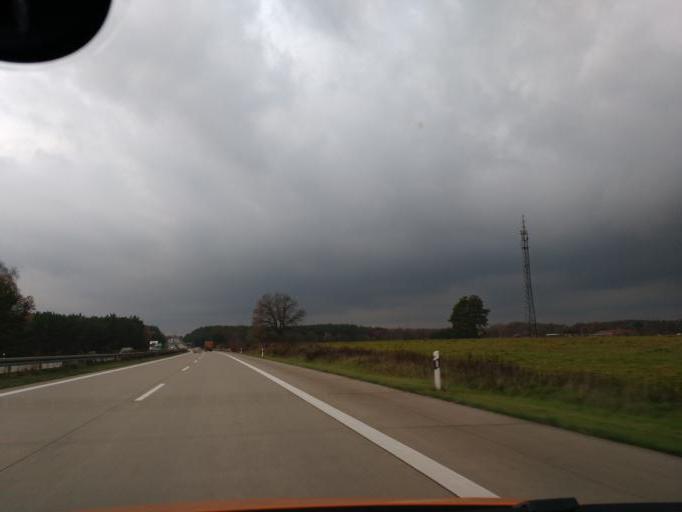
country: DE
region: Brandenburg
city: Heiligengrabe
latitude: 53.1694
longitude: 12.3585
